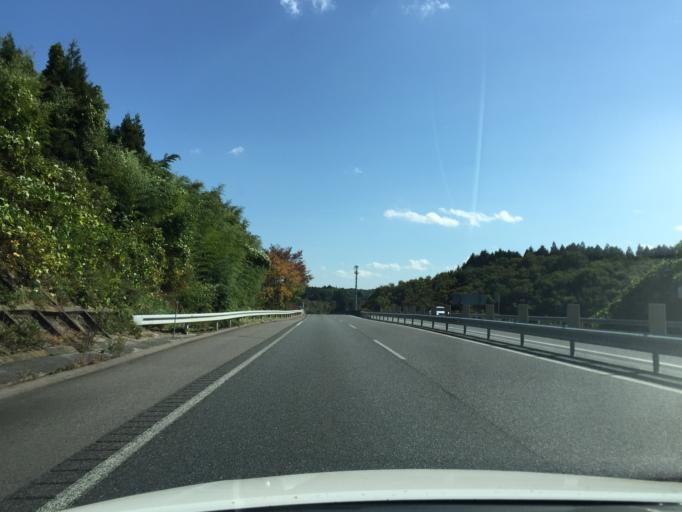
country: JP
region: Fukushima
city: Funehikimachi-funehiki
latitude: 37.2744
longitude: 140.6259
